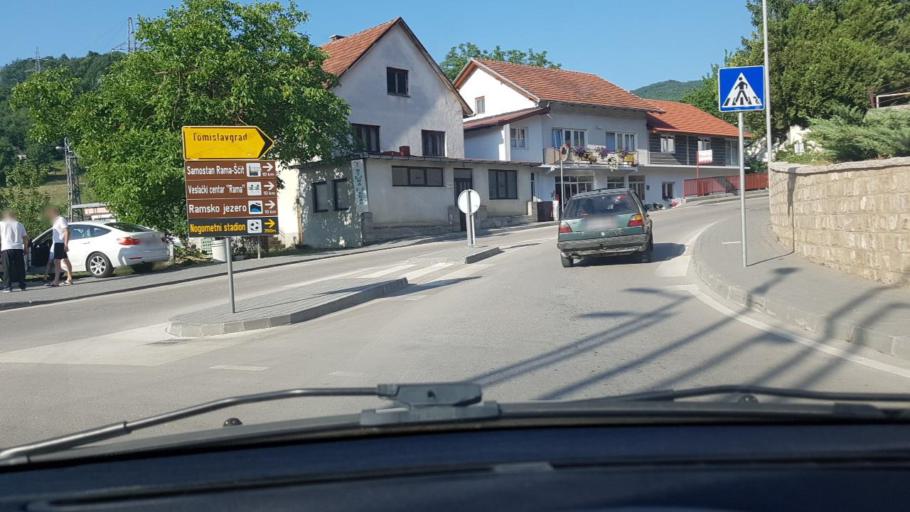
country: BA
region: Federation of Bosnia and Herzegovina
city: Prozor
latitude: 43.8231
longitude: 17.6076
